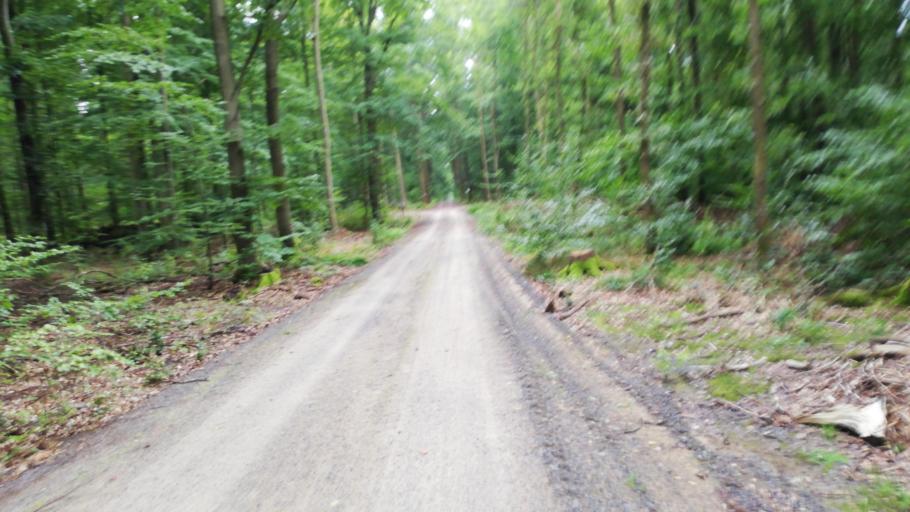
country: DE
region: Brandenburg
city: Rheinsberg
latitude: 53.1048
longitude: 12.8637
